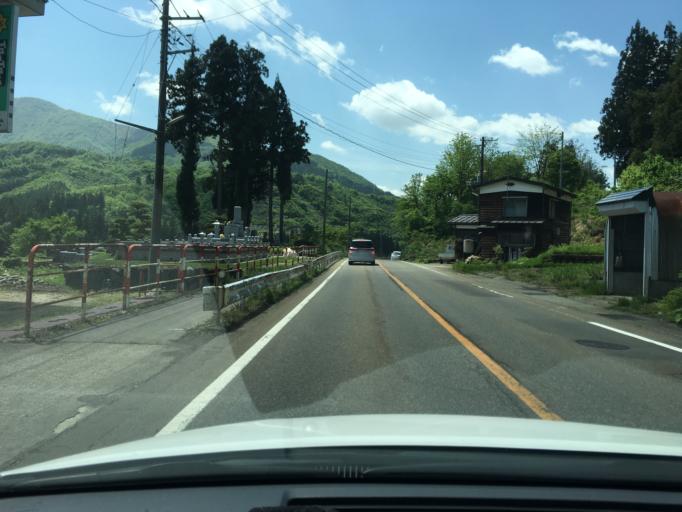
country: JP
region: Niigata
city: Tochio-honcho
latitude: 37.3110
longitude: 139.0128
